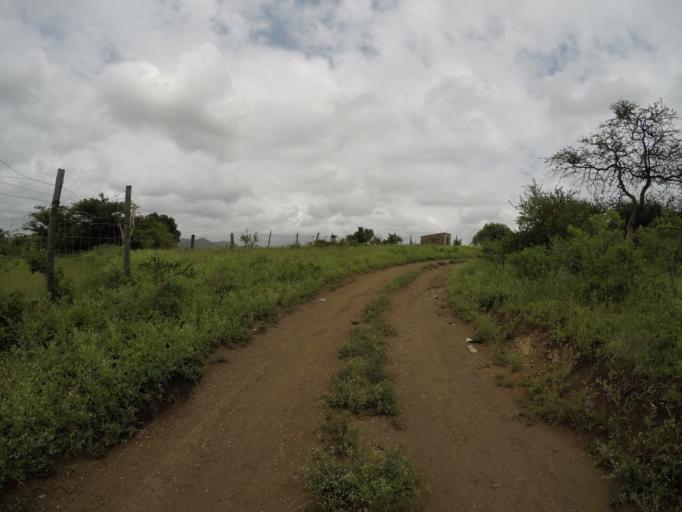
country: ZA
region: KwaZulu-Natal
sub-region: uThungulu District Municipality
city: Empangeni
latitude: -28.6082
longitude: 31.8928
